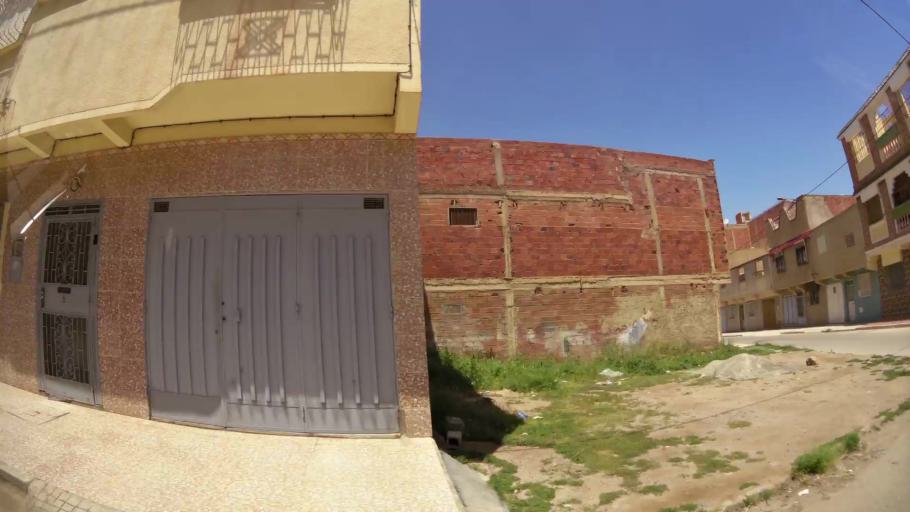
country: MA
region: Oriental
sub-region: Oujda-Angad
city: Oujda
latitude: 34.6883
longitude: -1.8926
